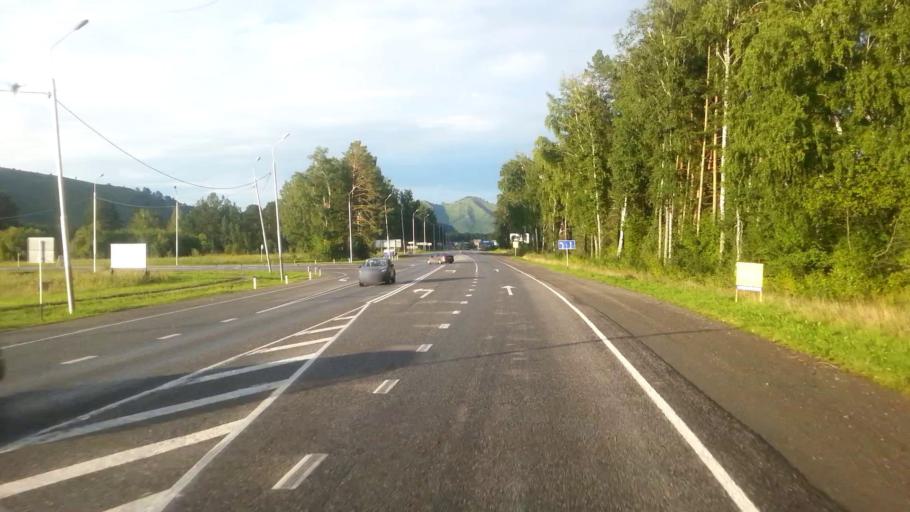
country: RU
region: Altay
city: Souzga
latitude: 51.8811
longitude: 85.8308
